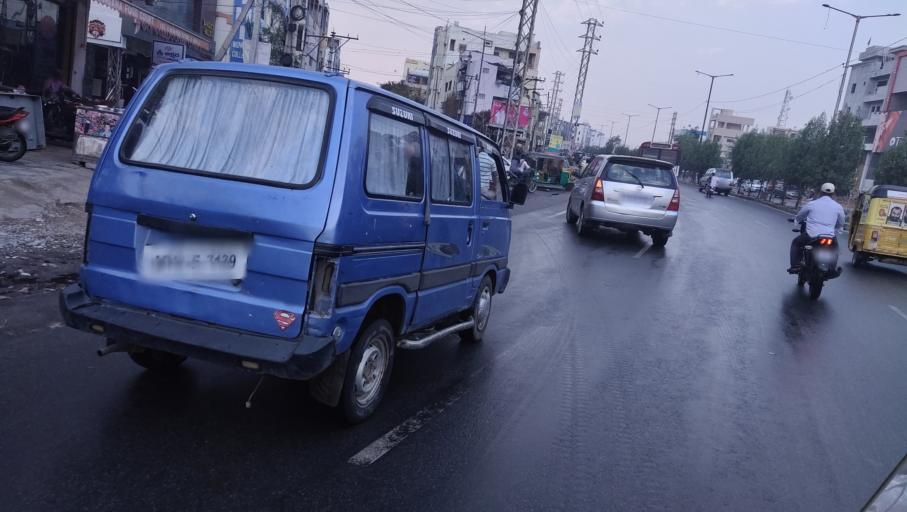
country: IN
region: Telangana
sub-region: Rangareddi
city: Lal Bahadur Nagar
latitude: 17.3216
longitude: 78.5601
